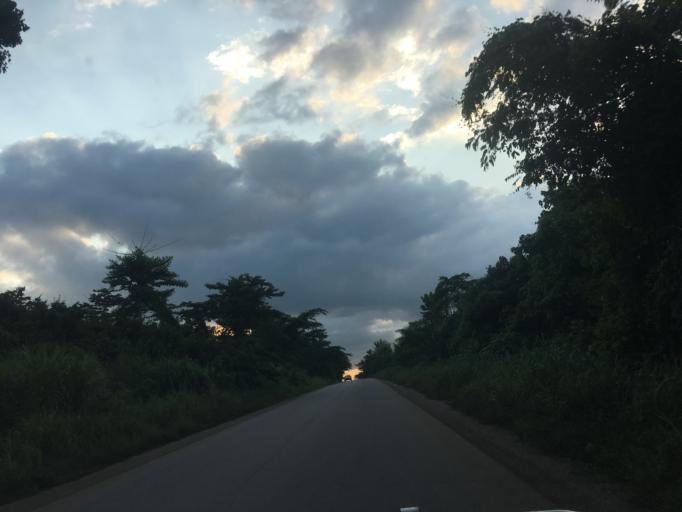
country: GH
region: Western
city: Bibiani
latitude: 6.7152
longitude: -2.4607
